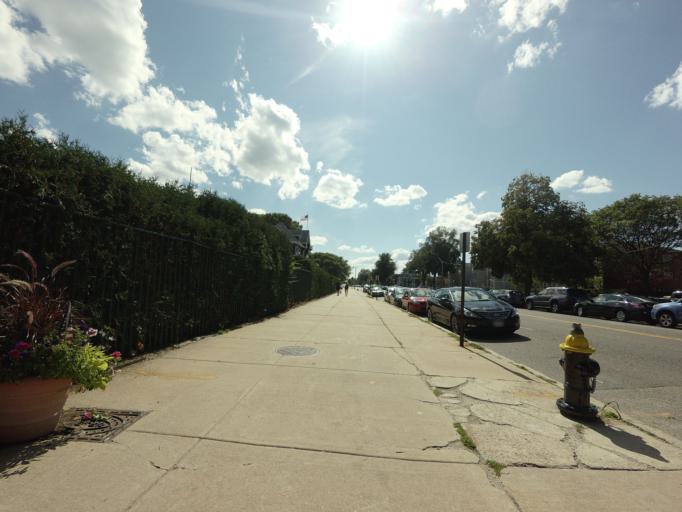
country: US
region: Massachusetts
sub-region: Suffolk County
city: South Boston
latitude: 42.3319
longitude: -71.0281
